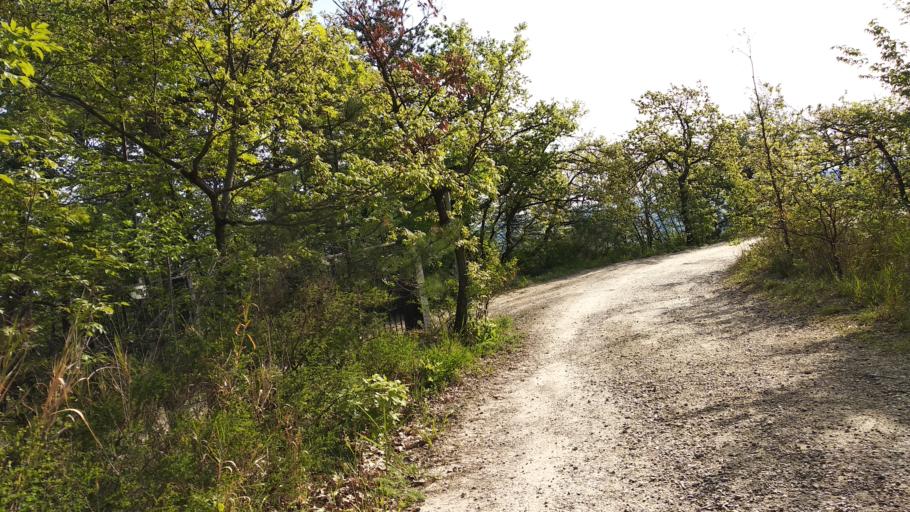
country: IT
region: Emilia-Romagna
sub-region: Provincia di Ravenna
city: Fognano
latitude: 44.2275
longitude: 11.7417
